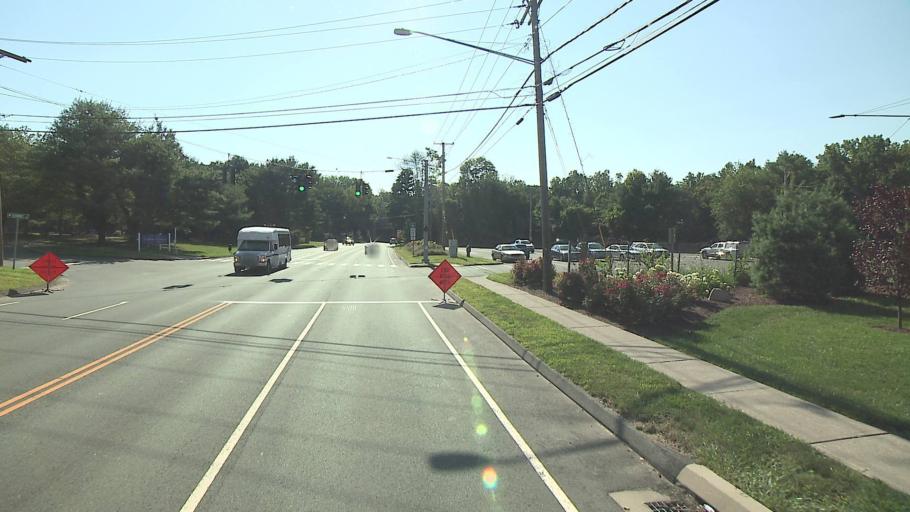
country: US
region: Connecticut
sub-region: Fairfield County
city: Trumbull
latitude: 41.2378
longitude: -73.1813
